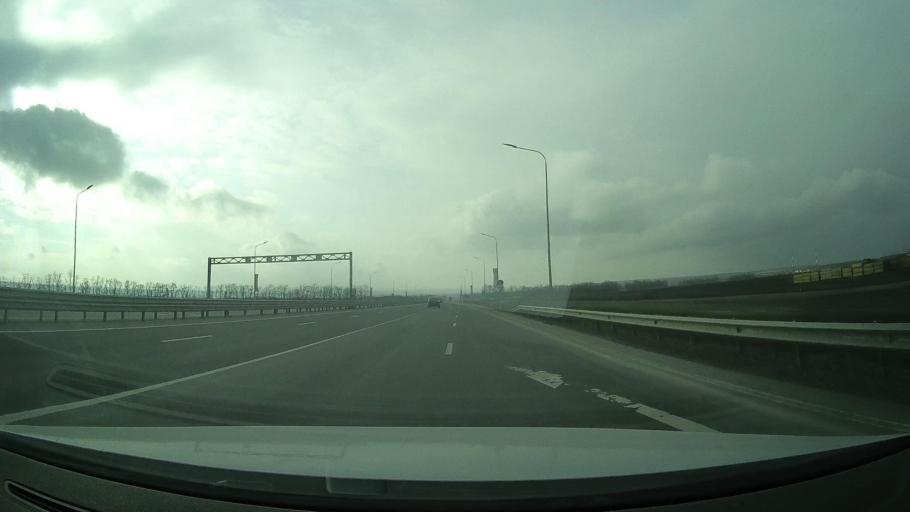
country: RU
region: Rostov
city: Grushevskaya
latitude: 47.4812
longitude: 39.9250
